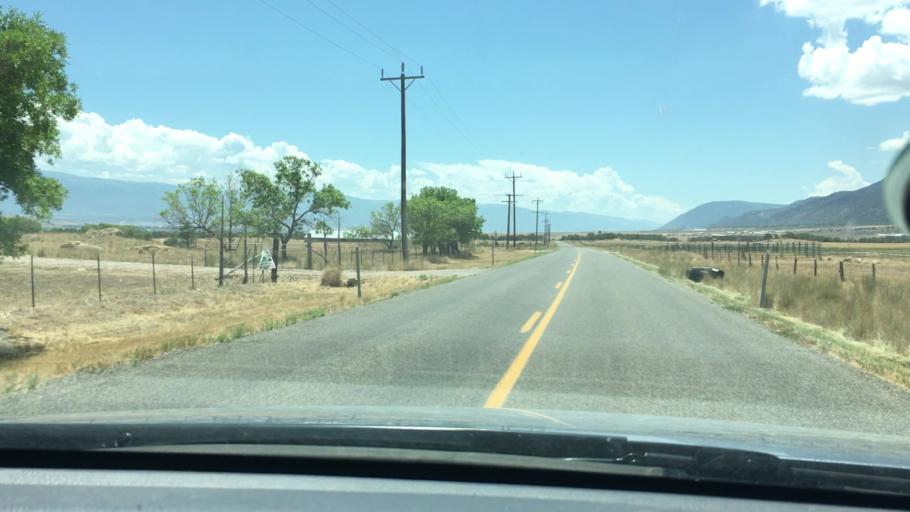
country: US
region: Utah
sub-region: Sanpete County
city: Fountain Green
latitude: 39.6000
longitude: -111.6435
